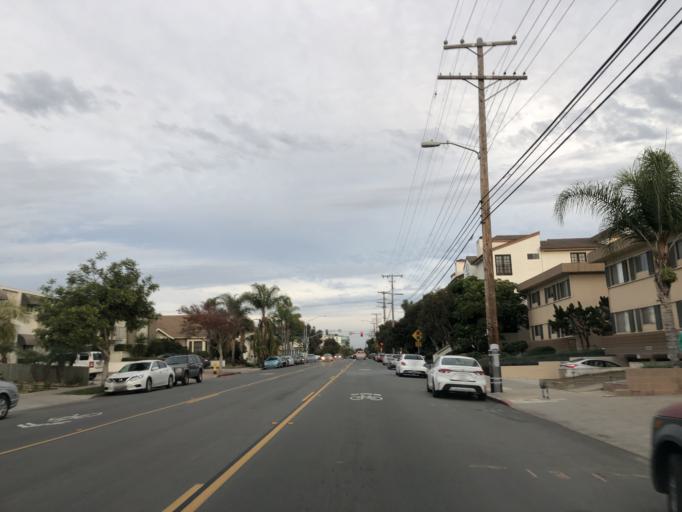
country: US
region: California
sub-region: San Diego County
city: San Diego
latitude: 32.7463
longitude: -117.1529
